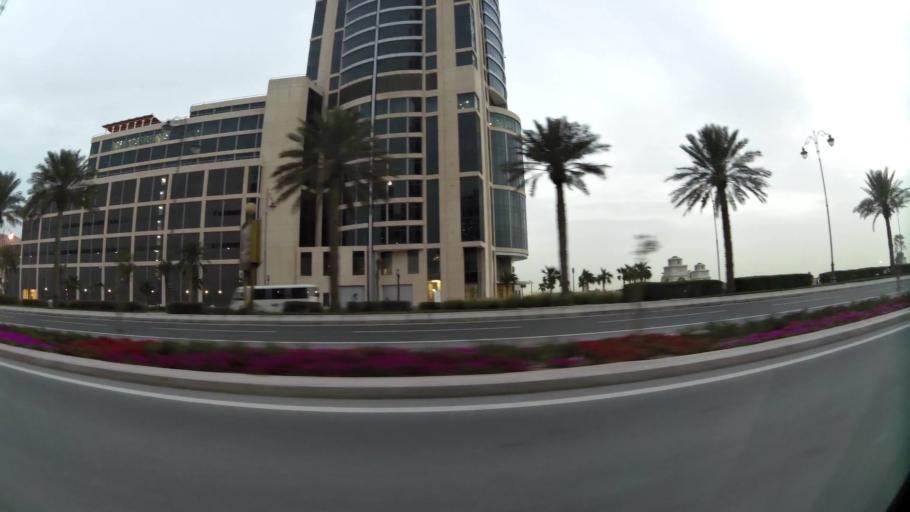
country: QA
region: Baladiyat ad Dawhah
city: Doha
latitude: 25.3723
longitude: 51.5332
